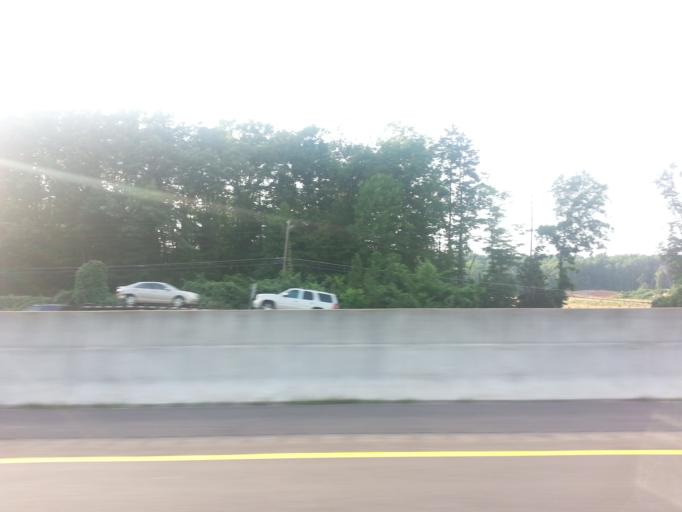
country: US
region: Tennessee
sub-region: Knox County
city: Farragut
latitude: 35.8938
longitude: -84.1946
